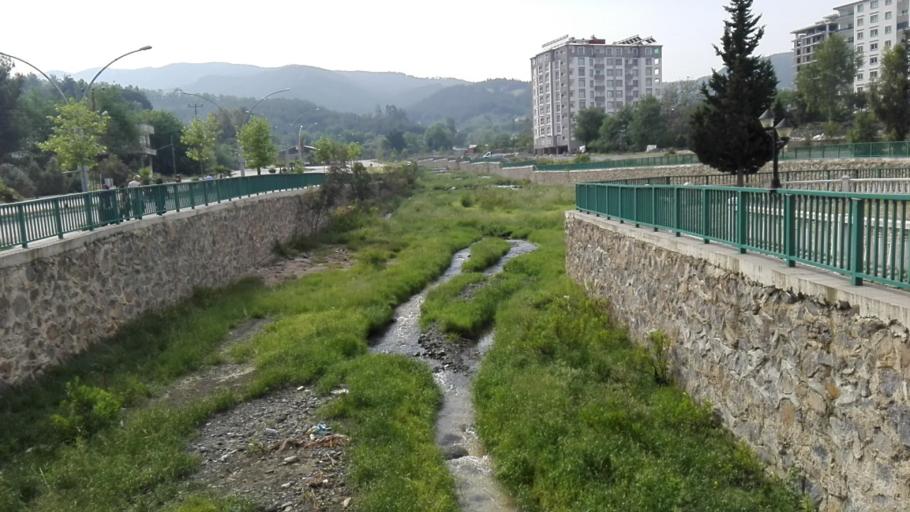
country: TR
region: Osmaniye
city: Haruniye
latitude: 37.2500
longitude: 36.4646
